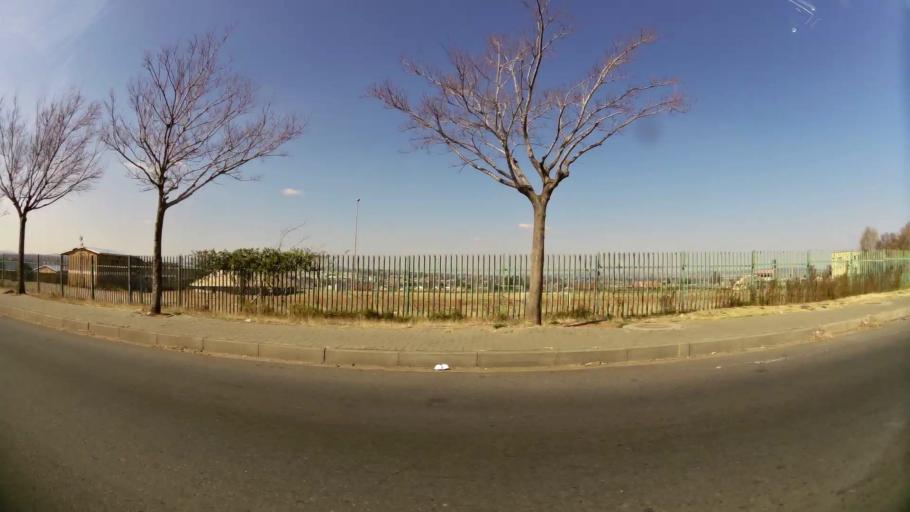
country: ZA
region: Gauteng
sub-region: City of Johannesburg Metropolitan Municipality
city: Soweto
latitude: -26.2729
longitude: 27.8731
